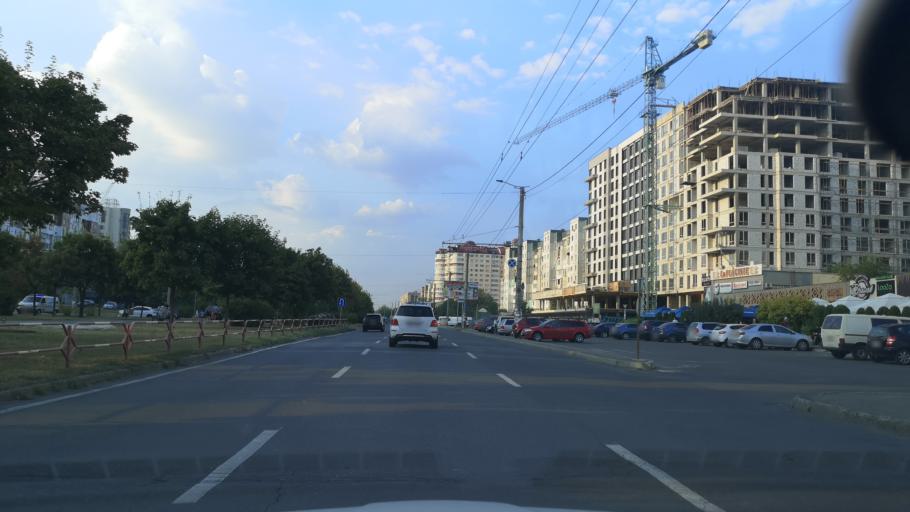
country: MD
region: Chisinau
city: Chisinau
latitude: 47.0439
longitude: 28.8906
